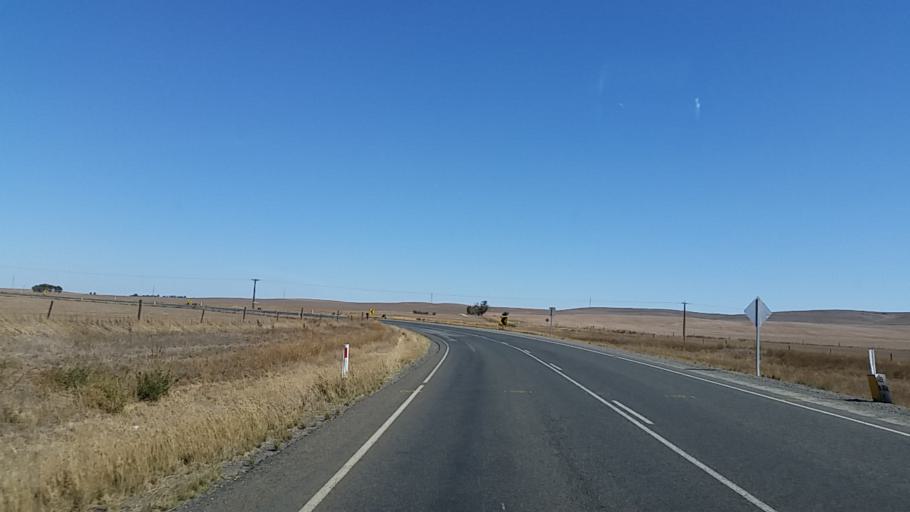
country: AU
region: South Australia
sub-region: Clare and Gilbert Valleys
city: Clare
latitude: -33.6826
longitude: 138.9075
